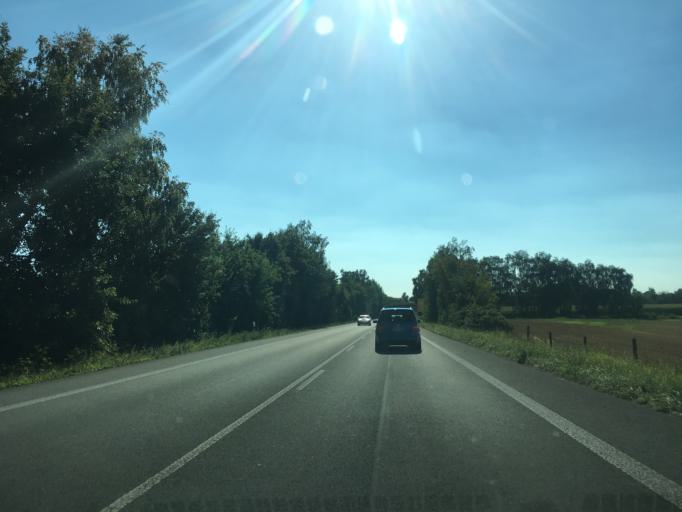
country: DE
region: North Rhine-Westphalia
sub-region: Regierungsbezirk Detmold
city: Rheda-Wiedenbruck
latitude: 51.8808
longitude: 8.2897
